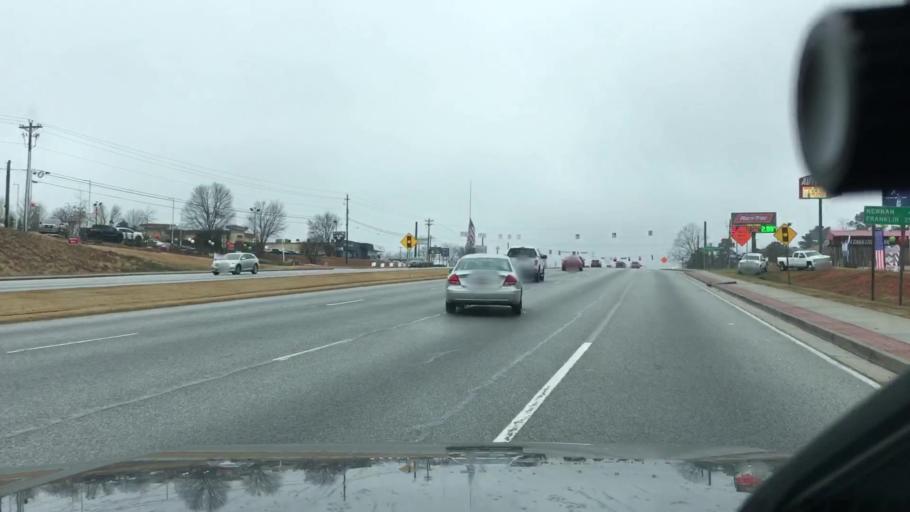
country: US
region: Georgia
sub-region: Coweta County
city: Newnan
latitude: 33.3969
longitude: -84.7510
